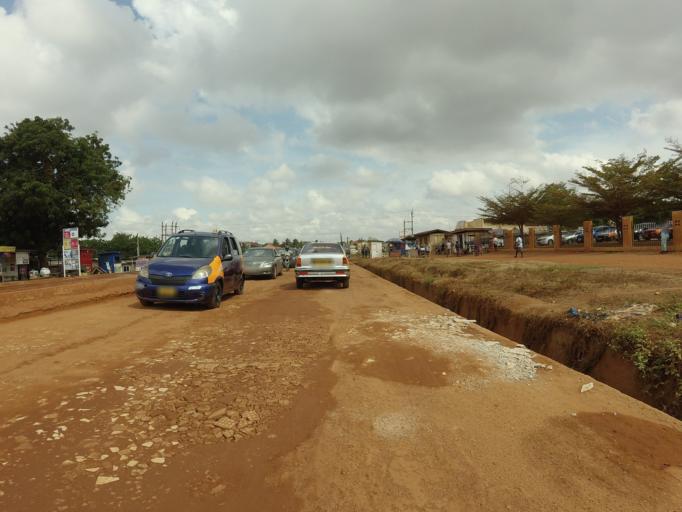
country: GH
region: Greater Accra
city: Teshi Old Town
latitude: 5.6026
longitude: -0.1208
